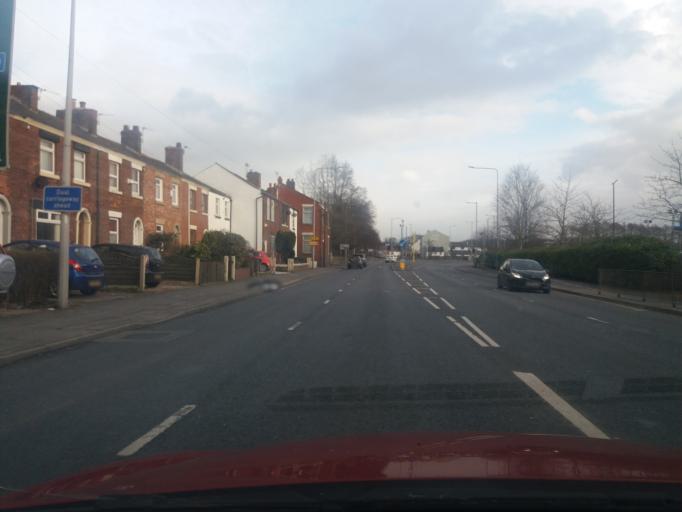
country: GB
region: England
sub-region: Lancashire
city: Preston
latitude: 53.7510
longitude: -2.6767
